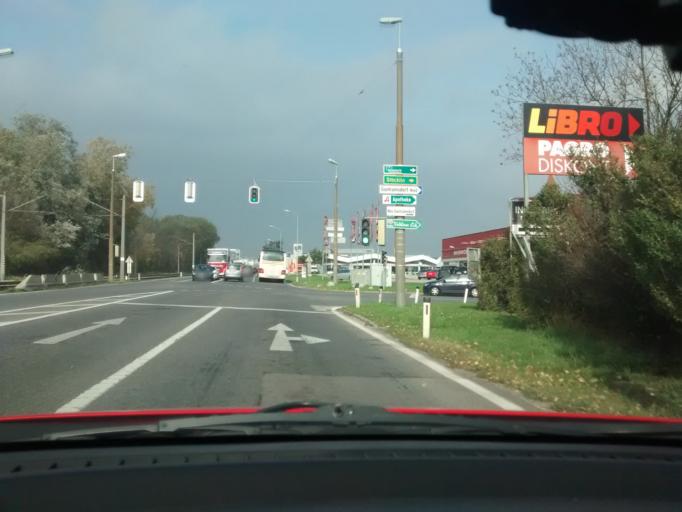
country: AT
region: Lower Austria
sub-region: Politischer Bezirk Modling
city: Neu-Guntramsdorf
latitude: 48.0679
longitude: 16.3128
